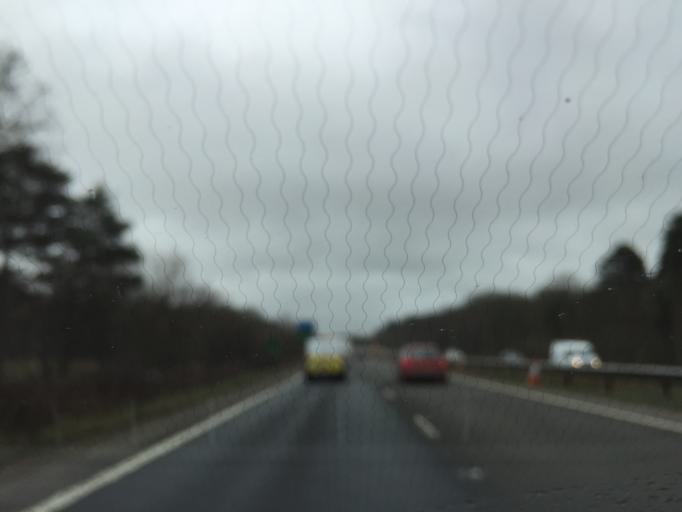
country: GB
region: England
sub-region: Hampshire
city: Cadnam
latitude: 50.9160
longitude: -1.5966
